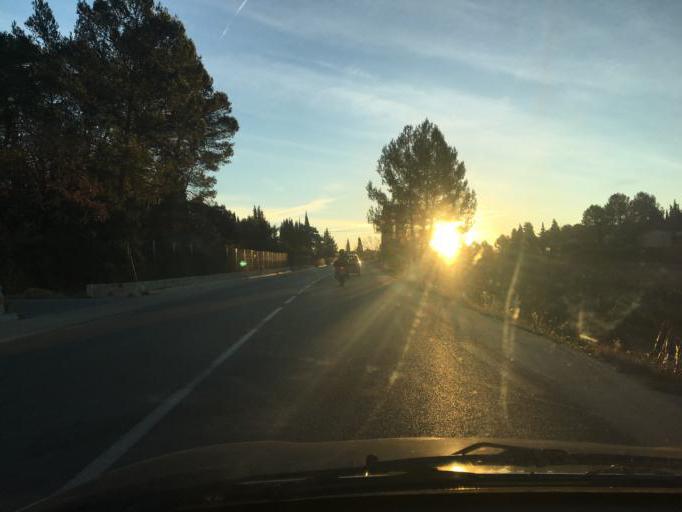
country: FR
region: Provence-Alpes-Cote d'Azur
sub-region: Departement du Var
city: Taradeau
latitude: 43.4659
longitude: 6.3925
